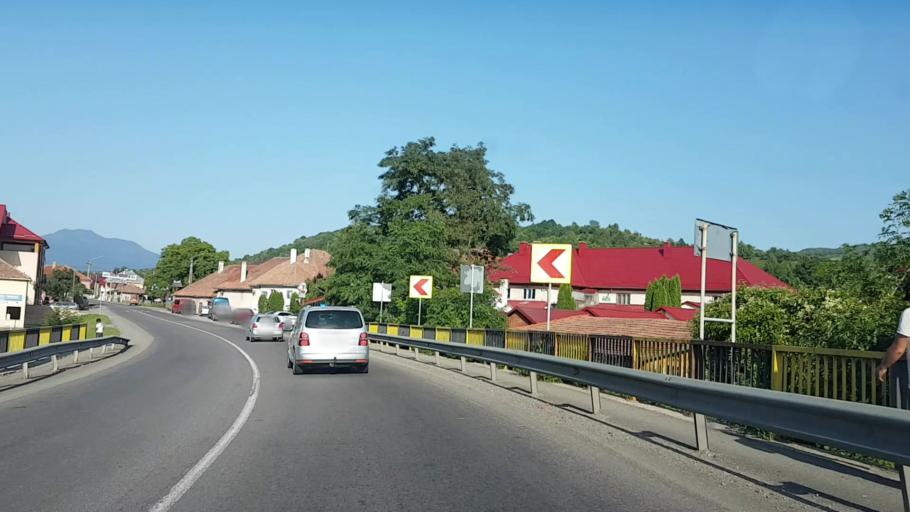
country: RO
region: Bistrita-Nasaud
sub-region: Comuna Josenii Bargaului
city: Josenii Bargaului
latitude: 47.2118
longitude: 24.6775
